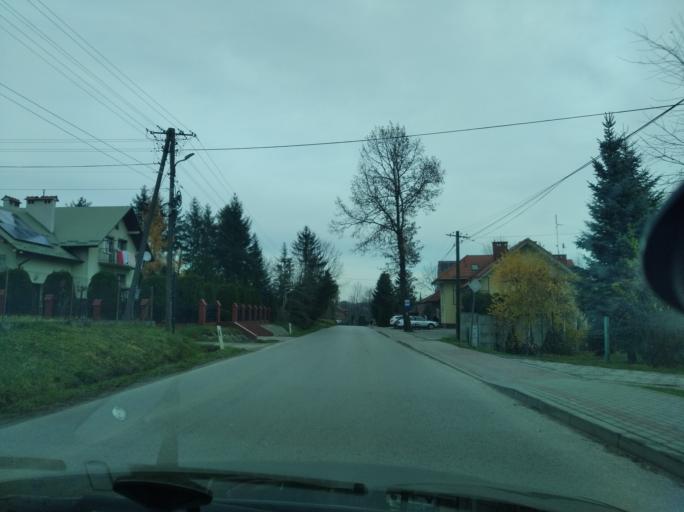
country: PL
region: Subcarpathian Voivodeship
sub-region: Powiat przeworski
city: Gac
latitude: 50.0265
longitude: 22.3580
